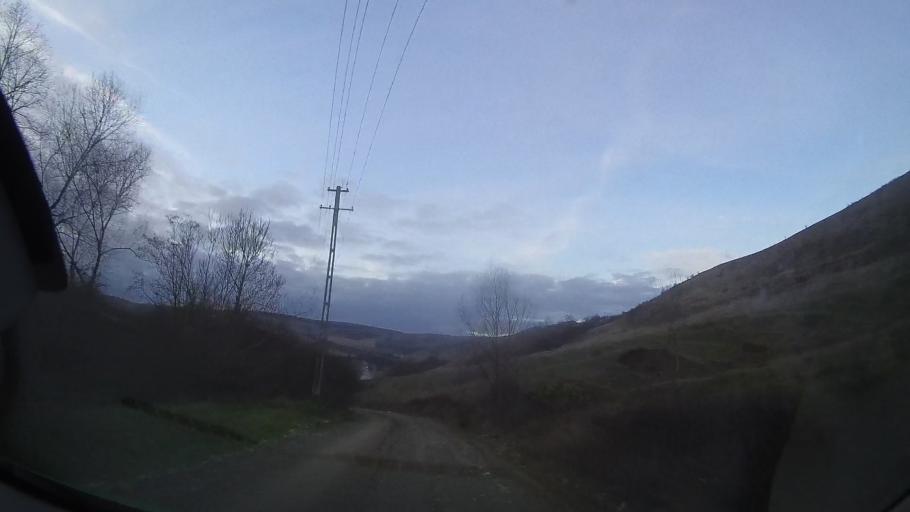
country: RO
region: Cluj
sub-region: Comuna Palatca
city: Palatca
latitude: 46.8634
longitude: 24.0210
